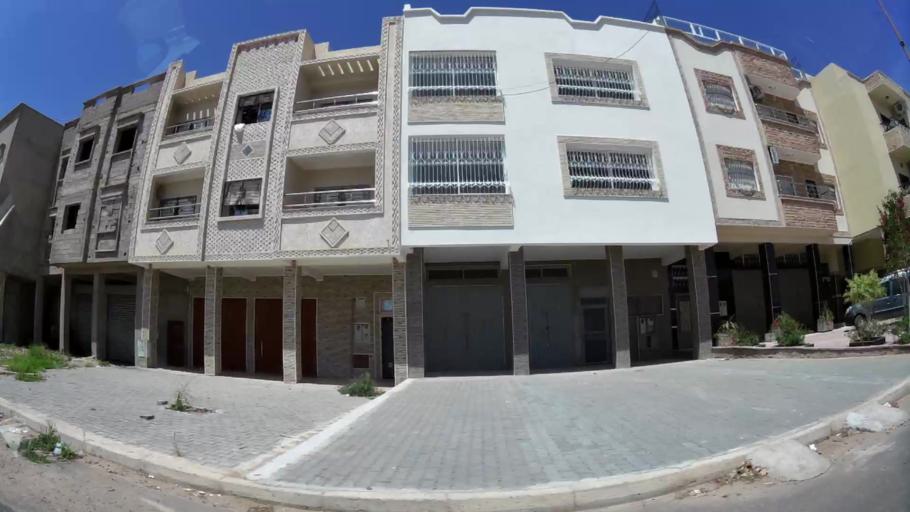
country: MA
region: Oued ed Dahab-Lagouira
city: Dakhla
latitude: 30.4256
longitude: -9.5526
